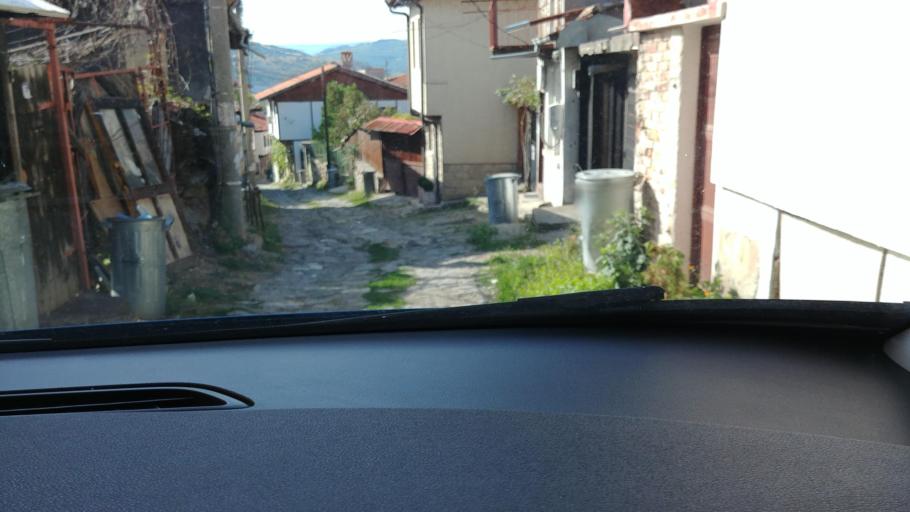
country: BG
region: Veliko Turnovo
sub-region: Obshtina Veliko Turnovo
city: Veliko Turnovo
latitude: 43.0854
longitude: 25.6402
